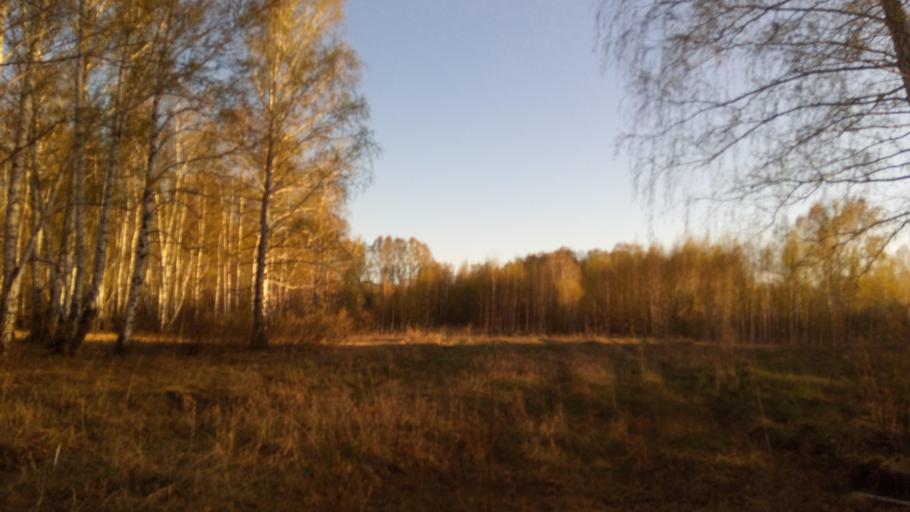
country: RU
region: Chelyabinsk
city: Timiryazevskiy
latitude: 54.9932
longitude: 60.8601
